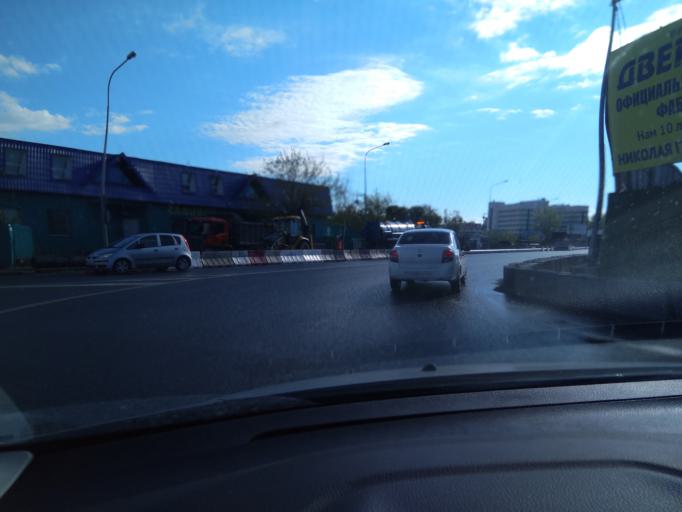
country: RU
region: Tjumen
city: Tyumen
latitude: 57.1384
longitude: 65.5142
